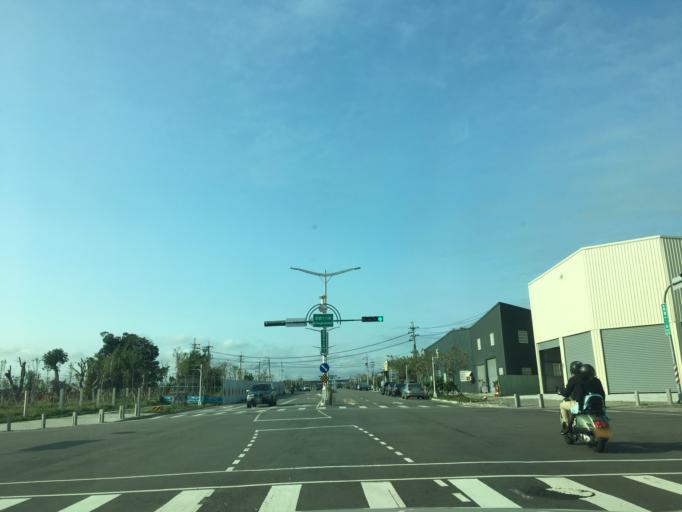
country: TW
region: Taiwan
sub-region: Taichung City
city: Taichung
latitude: 24.1888
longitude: 120.6933
